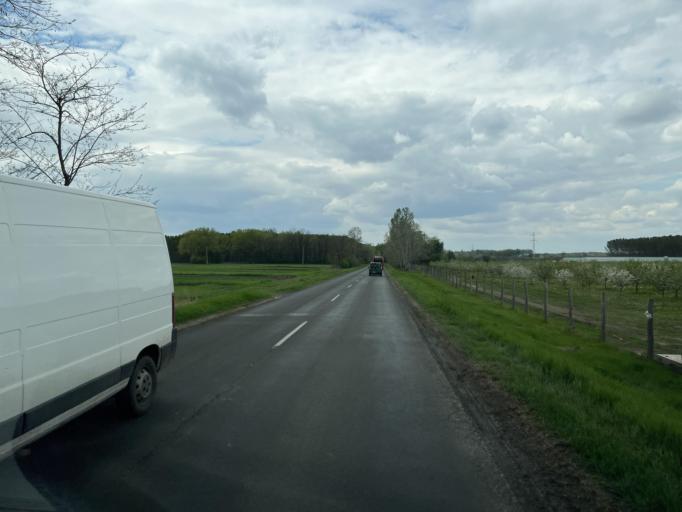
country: HU
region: Pest
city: Hernad
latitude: 47.1881
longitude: 19.4229
